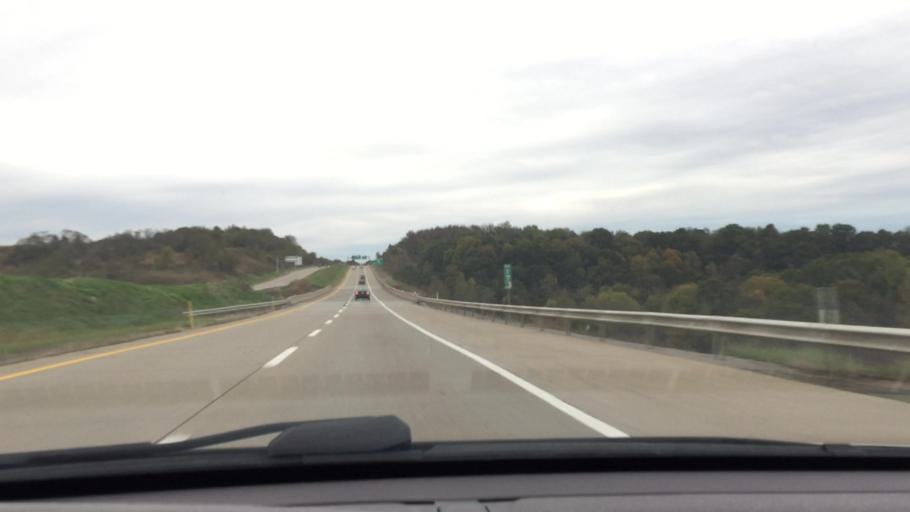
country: US
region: Pennsylvania
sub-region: Lawrence County
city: Oakland
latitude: 40.9560
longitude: -80.3946
